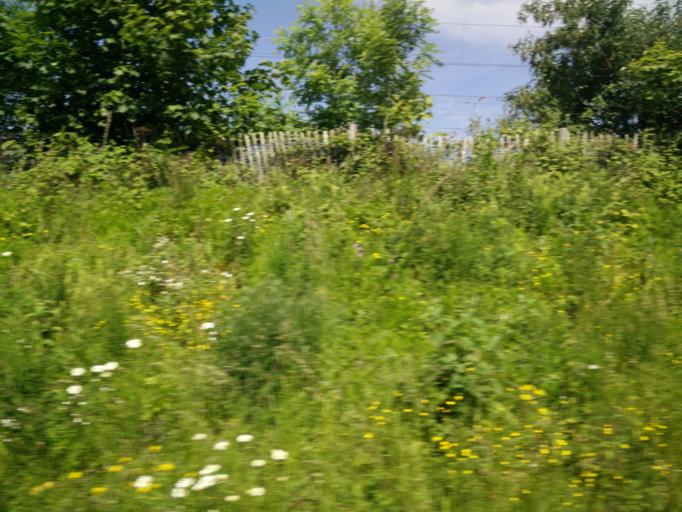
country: GB
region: England
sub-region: Luton
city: Luton
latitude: 51.8813
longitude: -0.4098
